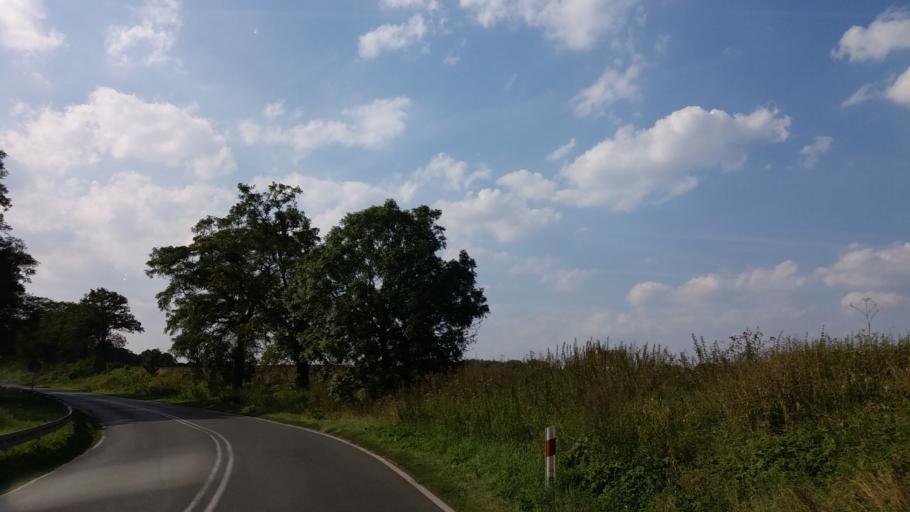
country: PL
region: West Pomeranian Voivodeship
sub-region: Powiat choszczenski
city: Choszczno
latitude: 53.1476
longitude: 15.4498
